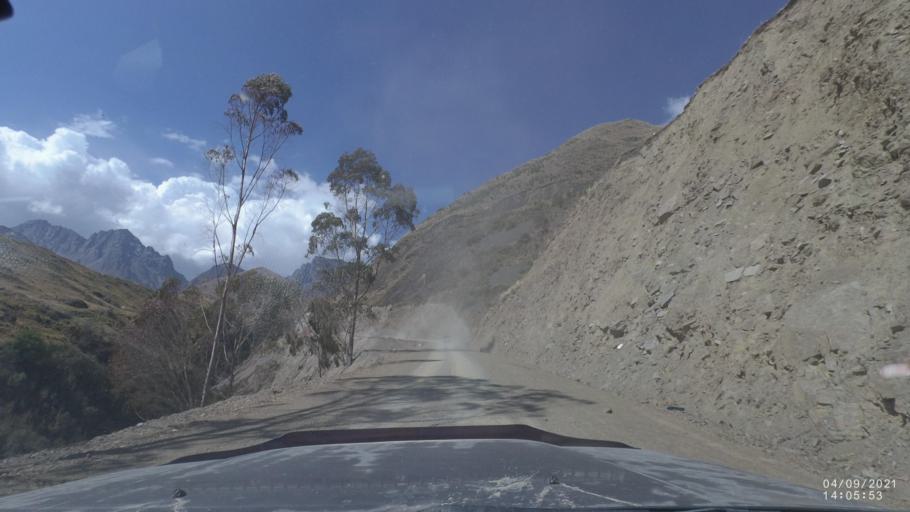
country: BO
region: Cochabamba
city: Sipe Sipe
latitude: -17.2322
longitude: -66.4737
